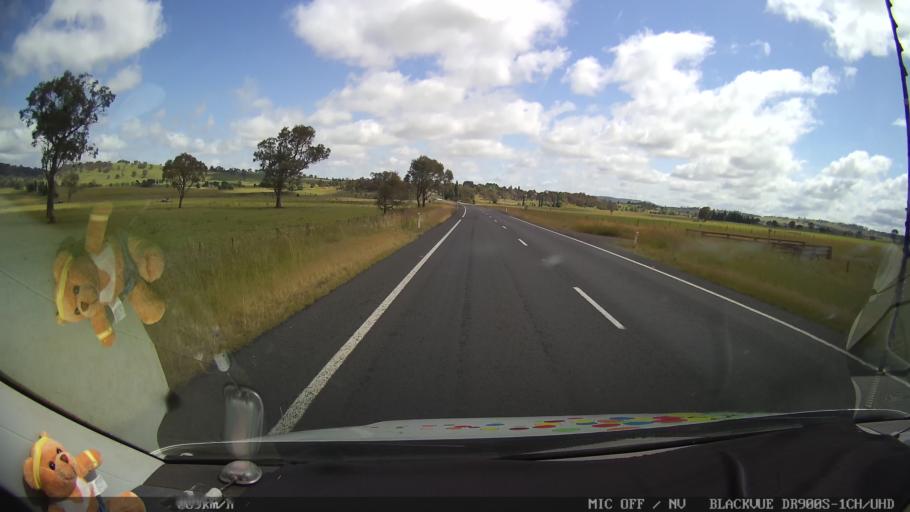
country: AU
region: New South Wales
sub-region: Glen Innes Severn
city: Glen Innes
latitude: -29.9398
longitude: 151.7231
